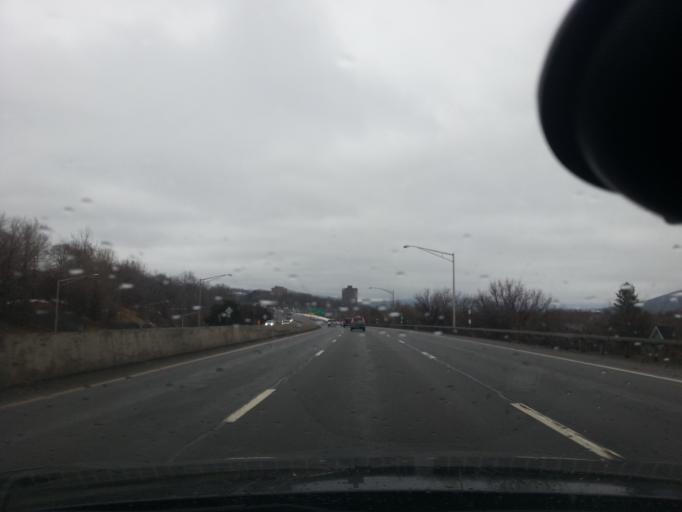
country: US
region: New York
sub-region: Onondaga County
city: Syracuse
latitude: 43.0193
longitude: -76.1405
